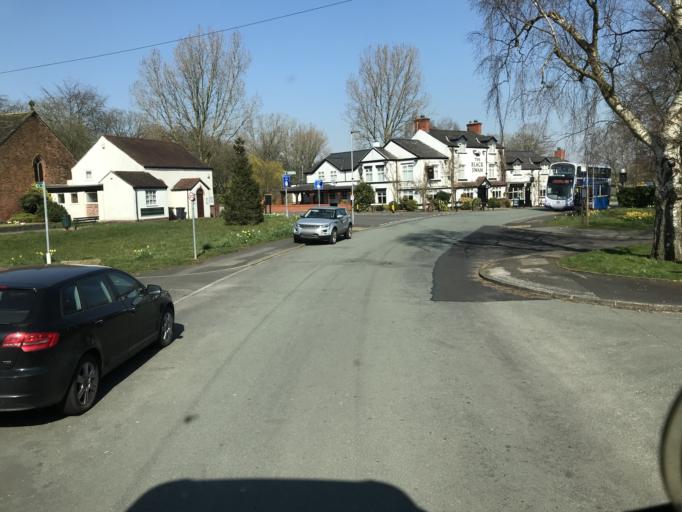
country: GB
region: England
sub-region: Trafford
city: Partington
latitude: 53.4157
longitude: -2.4563
